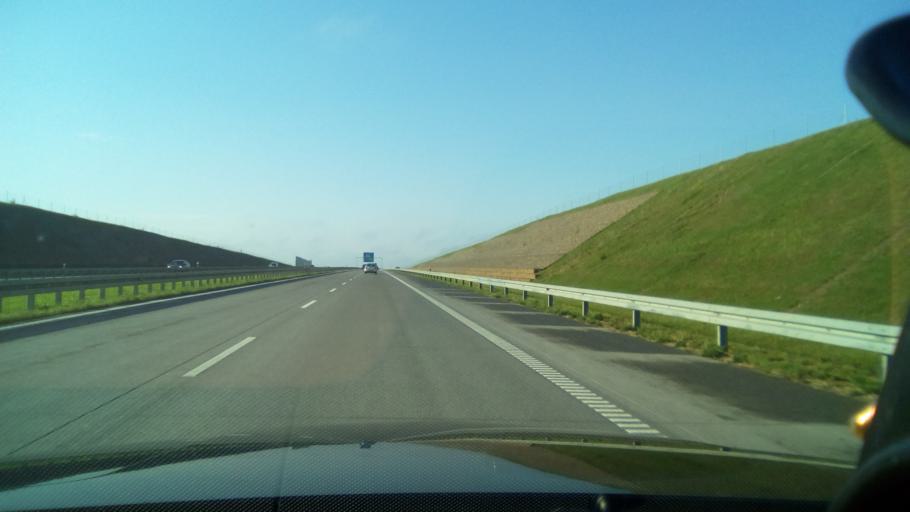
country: PL
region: Silesian Voivodeship
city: Wozniki
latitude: 50.6210
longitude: 19.0318
